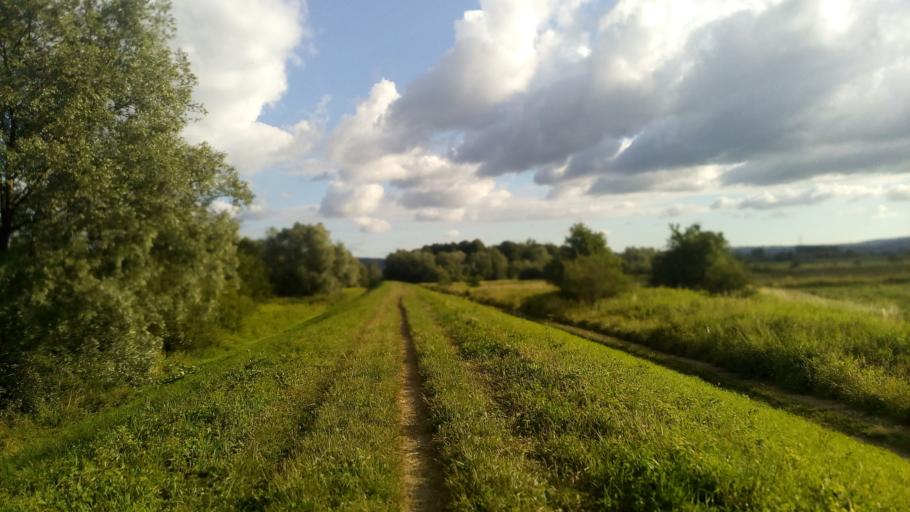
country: PL
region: Lesser Poland Voivodeship
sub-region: Powiat nowosadecki
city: Stary Sacz
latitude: 49.5850
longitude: 20.6542
